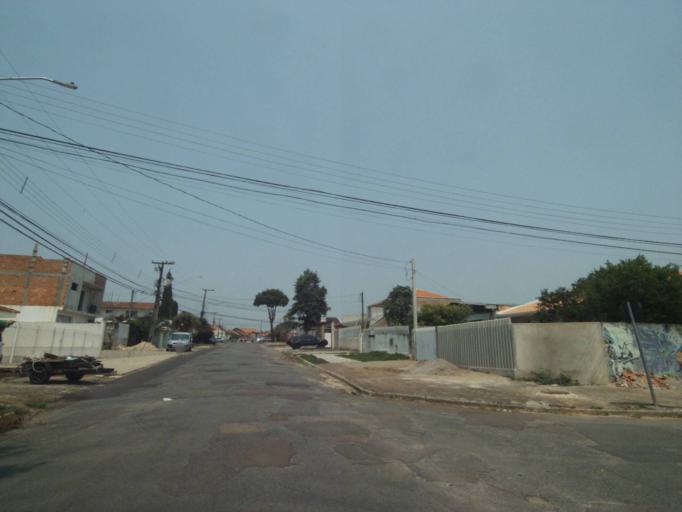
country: BR
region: Parana
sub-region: Sao Jose Dos Pinhais
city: Sao Jose dos Pinhais
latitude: -25.5311
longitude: -49.2398
